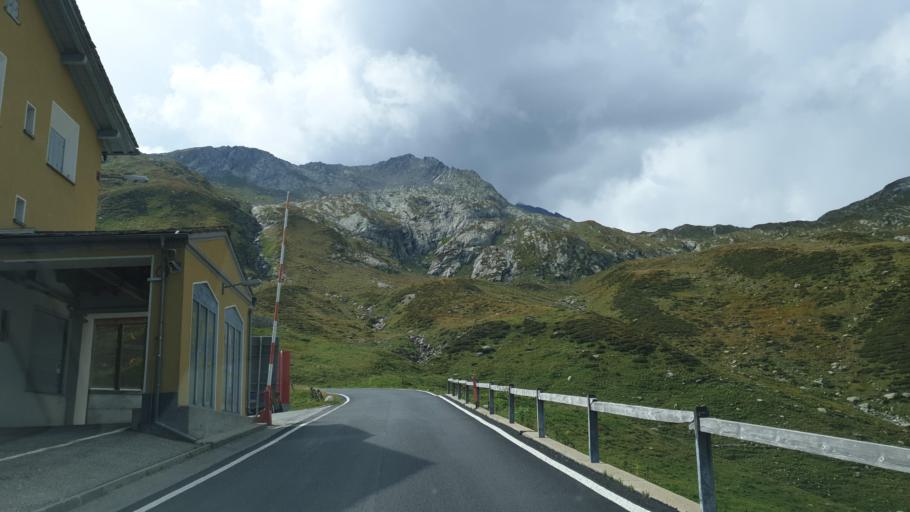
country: IT
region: Lombardy
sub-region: Provincia di Sondrio
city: Campodolcino
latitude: 46.5120
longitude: 9.3271
